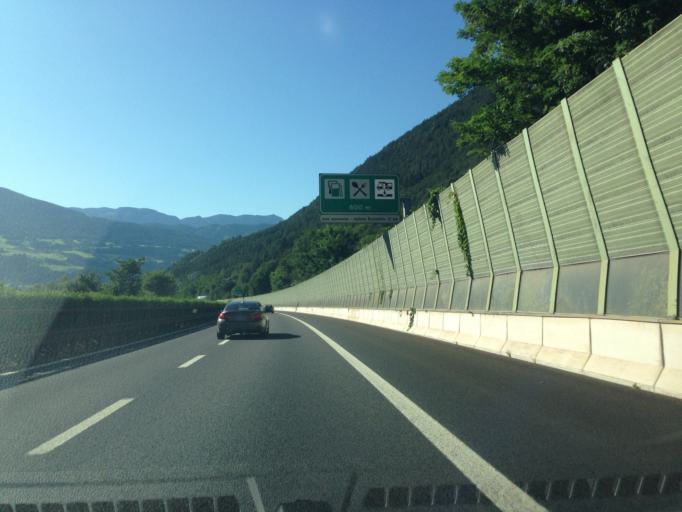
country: IT
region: Trentino-Alto Adige
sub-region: Bolzano
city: Varna
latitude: 46.7371
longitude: 11.6393
